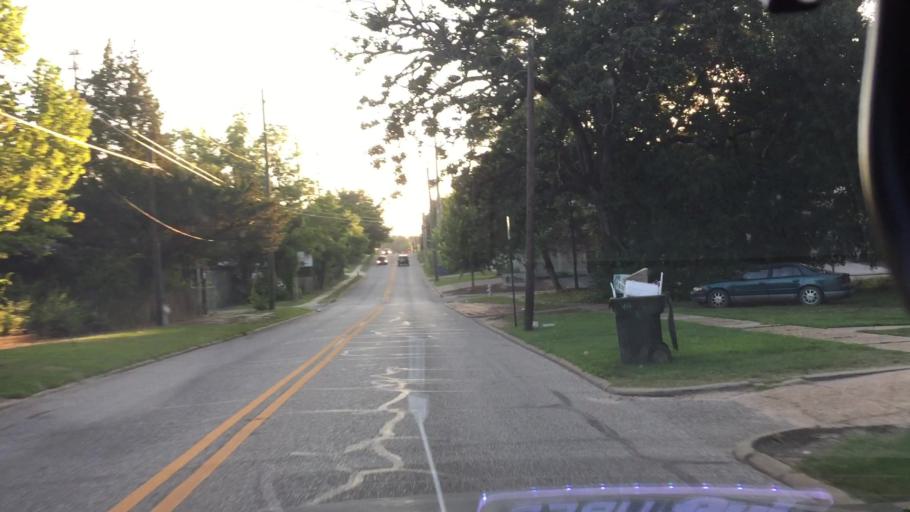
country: US
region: Alabama
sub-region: Lee County
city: Auburn
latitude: 32.6110
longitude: -85.4839
